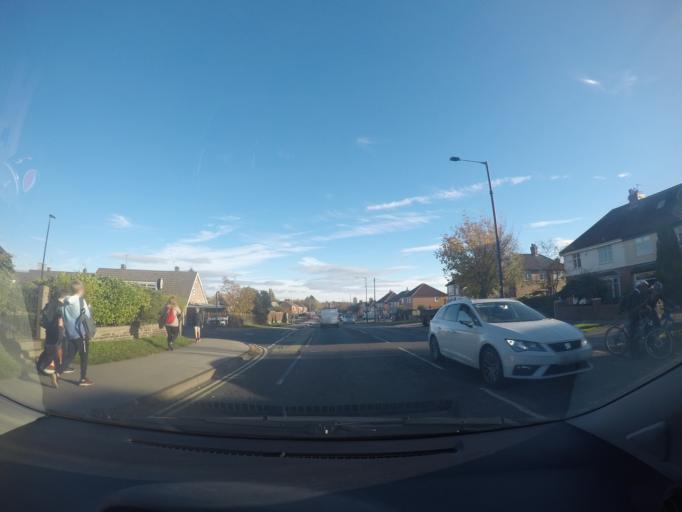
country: GB
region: England
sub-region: City of York
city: Nether Poppleton
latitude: 53.9676
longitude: -1.1292
